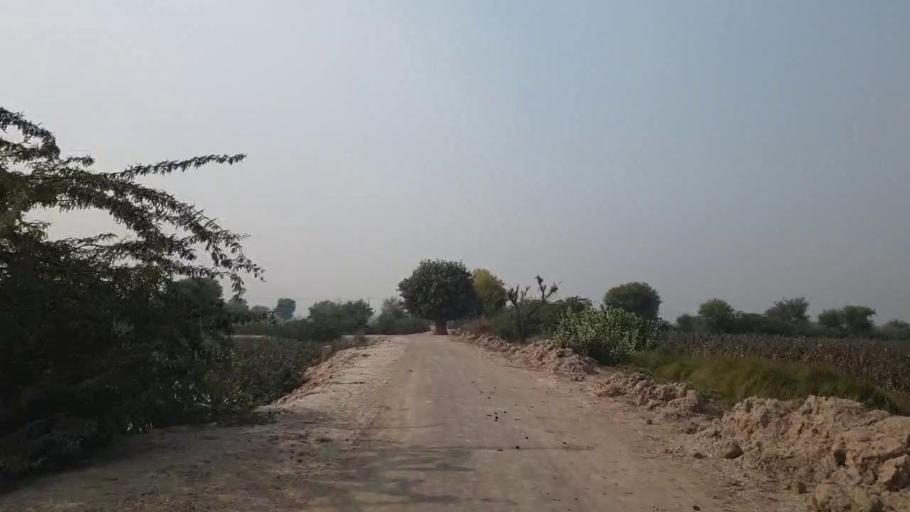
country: PK
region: Sindh
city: Bhan
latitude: 26.5411
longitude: 67.7176
